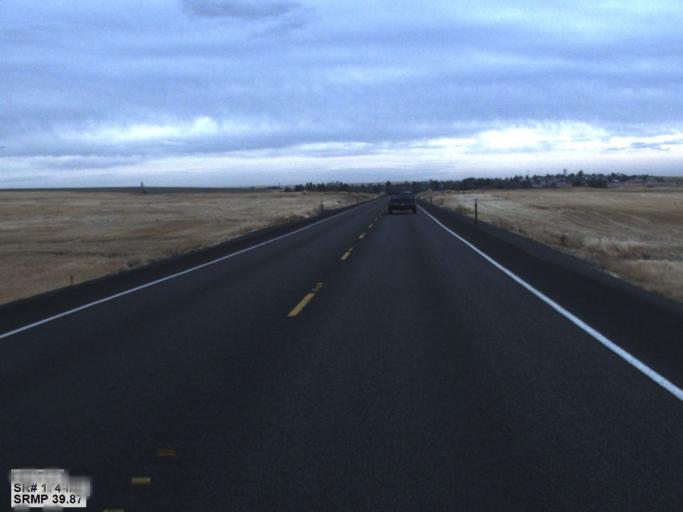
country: US
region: Washington
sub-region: Okanogan County
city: Coulee Dam
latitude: 47.7801
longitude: -118.7326
